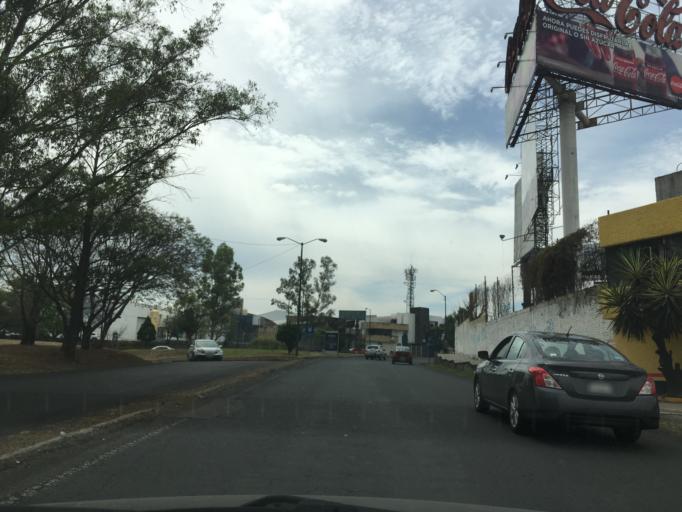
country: MX
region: Michoacan
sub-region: Morelia
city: Morelos
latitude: 19.6765
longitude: -101.2206
